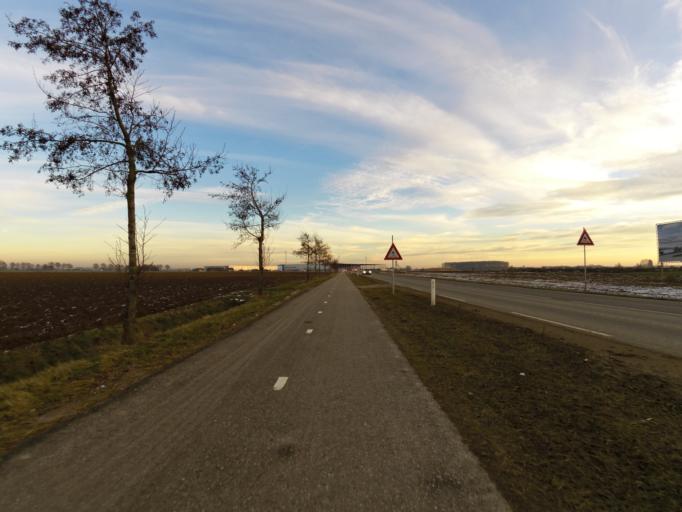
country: NL
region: Gelderland
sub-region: Gemeente Montferland
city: s-Heerenberg
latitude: 51.8771
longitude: 6.2809
